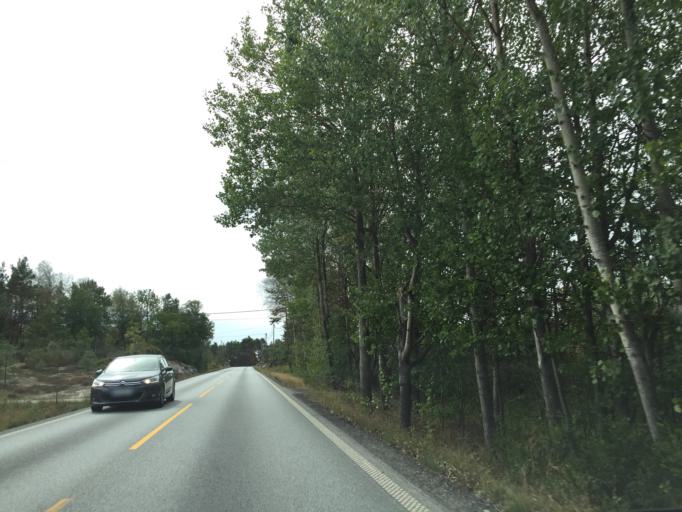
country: NO
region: Ostfold
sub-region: Hvaler
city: Skjaerhalden
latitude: 59.0729
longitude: 10.9361
